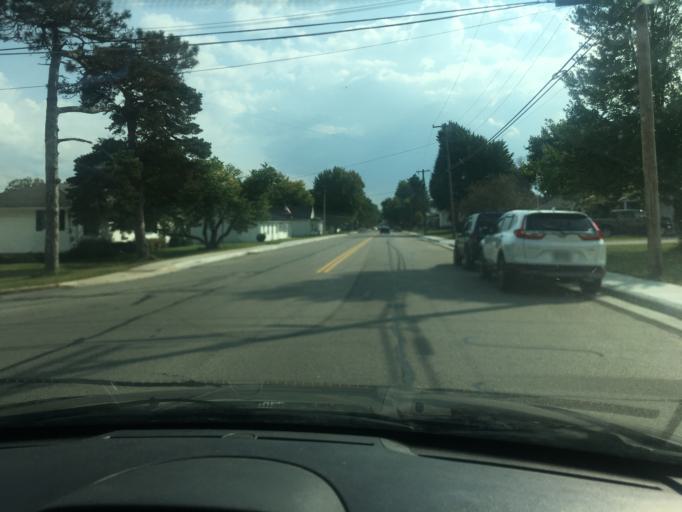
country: US
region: Ohio
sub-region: Champaign County
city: Urbana
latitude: 40.1161
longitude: -83.7644
